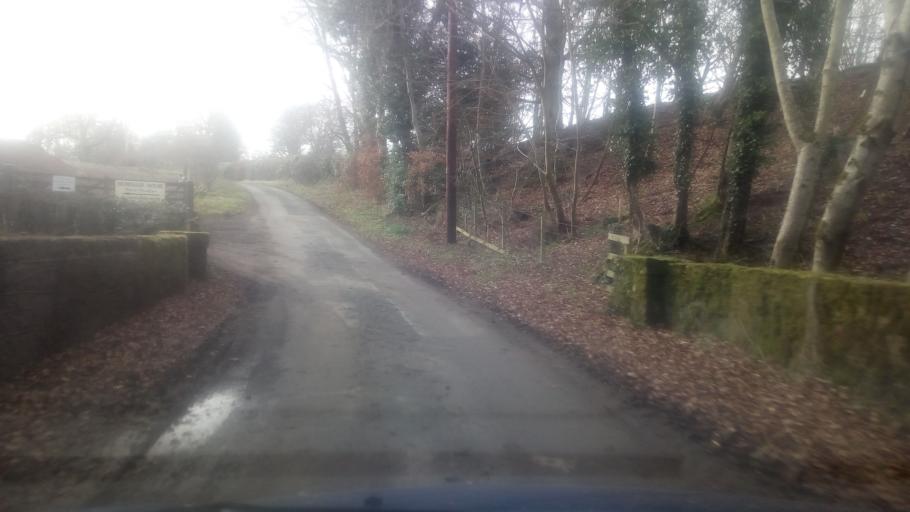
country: GB
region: Scotland
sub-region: The Scottish Borders
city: Jedburgh
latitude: 55.4626
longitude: -2.5620
